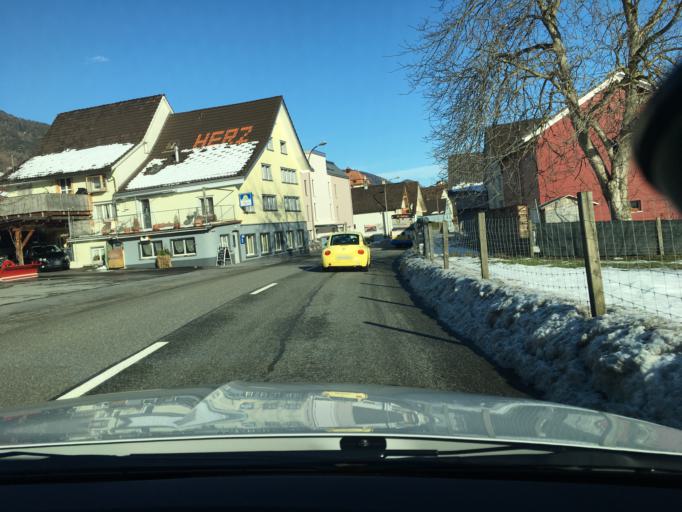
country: CH
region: Saint Gallen
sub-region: Wahlkreis Rheintal
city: Altstatten
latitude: 47.3853
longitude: 9.5504
